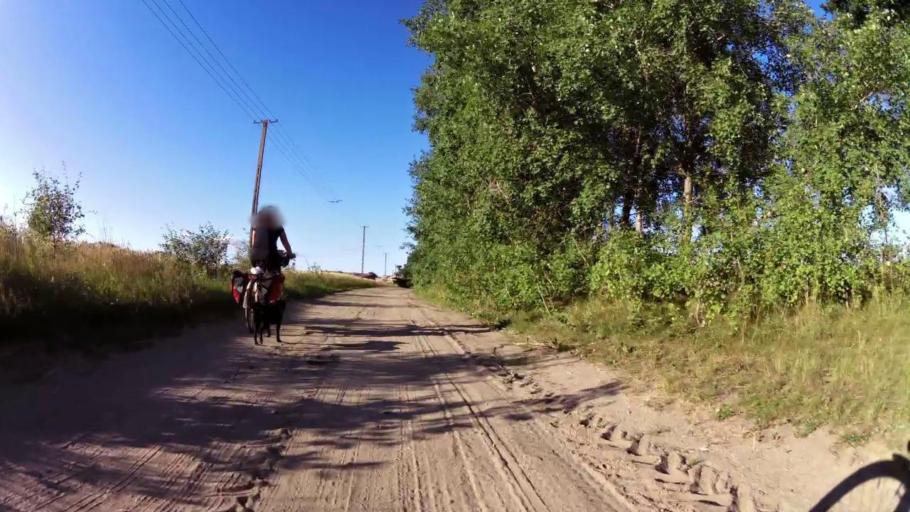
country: PL
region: West Pomeranian Voivodeship
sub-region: Powiat swidwinski
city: Swidwin
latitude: 53.7276
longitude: 15.8393
